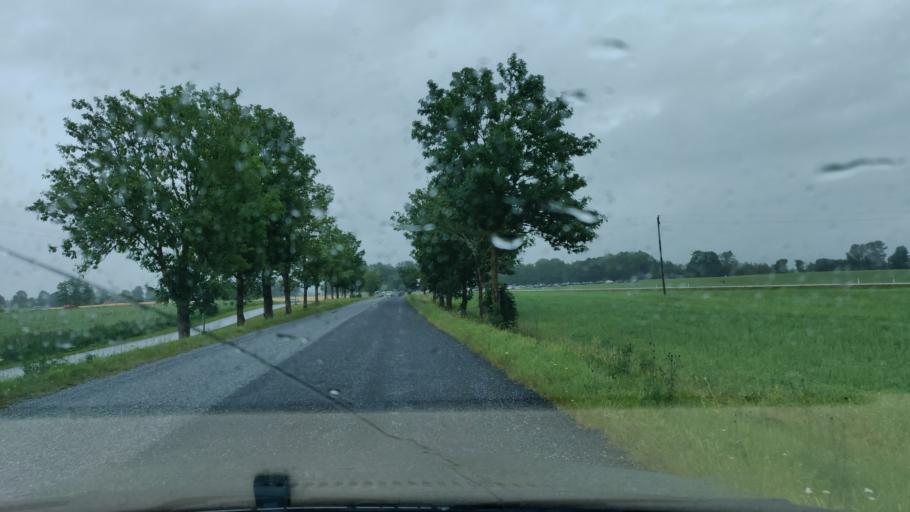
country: EE
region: Jaervamaa
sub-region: Jaerva-Jaani vald
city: Jarva-Jaani
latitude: 59.0940
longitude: 25.6905
